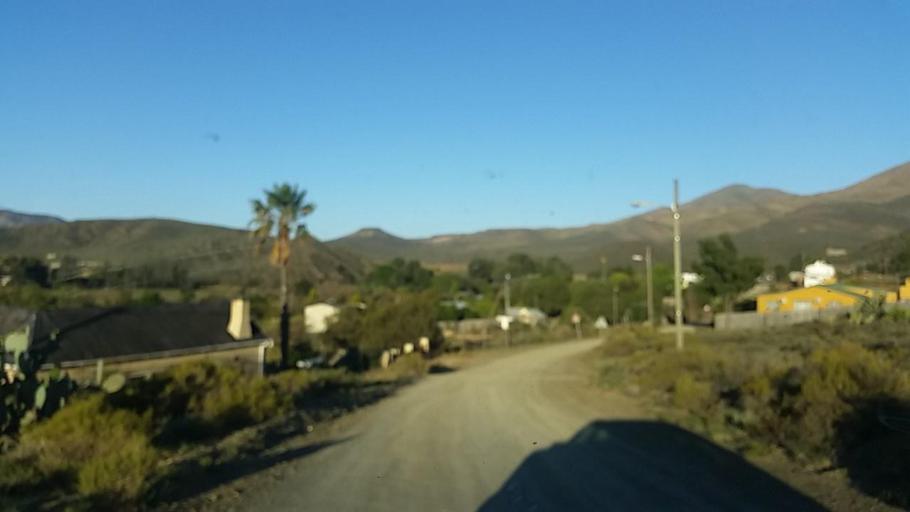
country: ZA
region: Western Cape
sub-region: Eden District Municipality
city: Knysna
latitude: -33.6558
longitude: 23.1309
